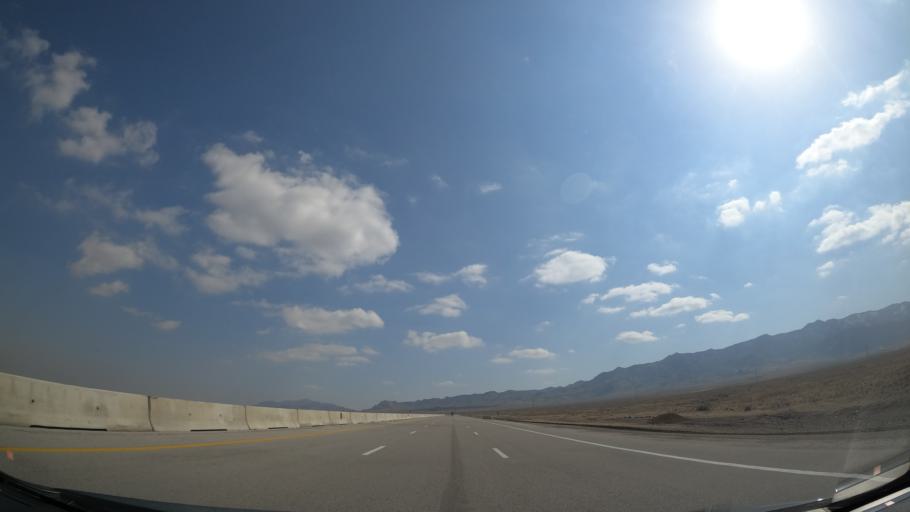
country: IR
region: Alborz
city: Eshtehard
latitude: 35.7226
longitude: 50.5675
